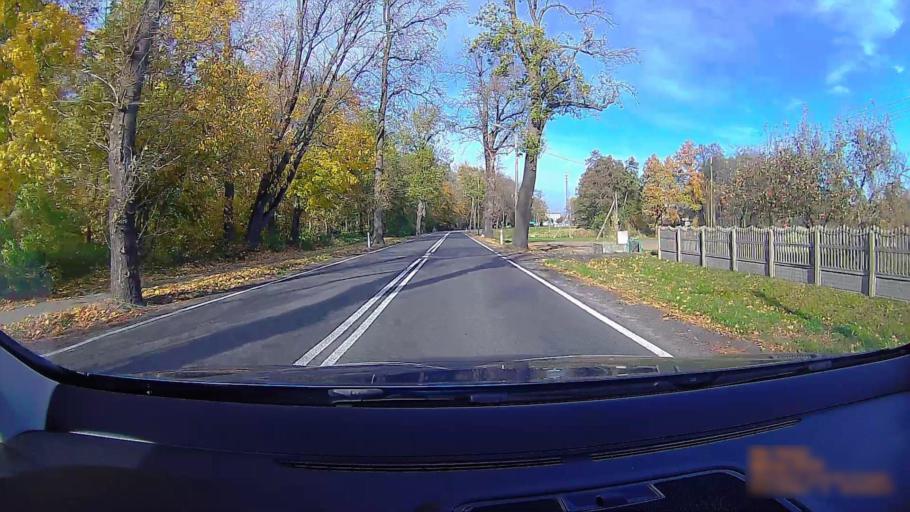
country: PL
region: Greater Poland Voivodeship
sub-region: Powiat ostrzeszowski
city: Doruchow
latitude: 51.4133
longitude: 18.0761
